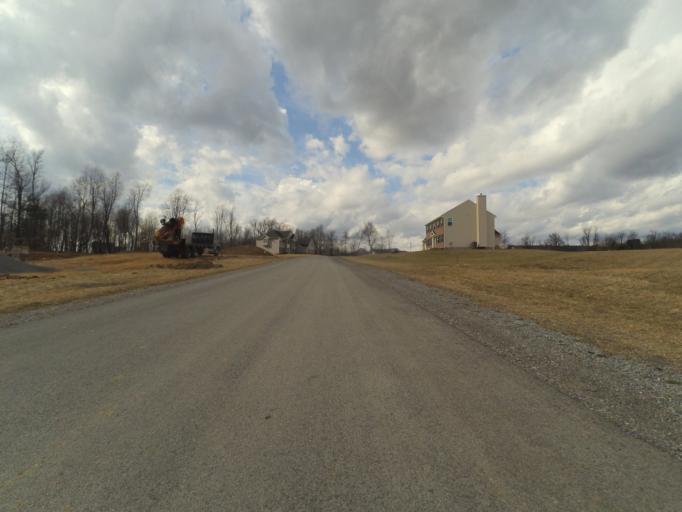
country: US
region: Pennsylvania
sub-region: Centre County
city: Stormstown
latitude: 40.7987
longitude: -77.9936
